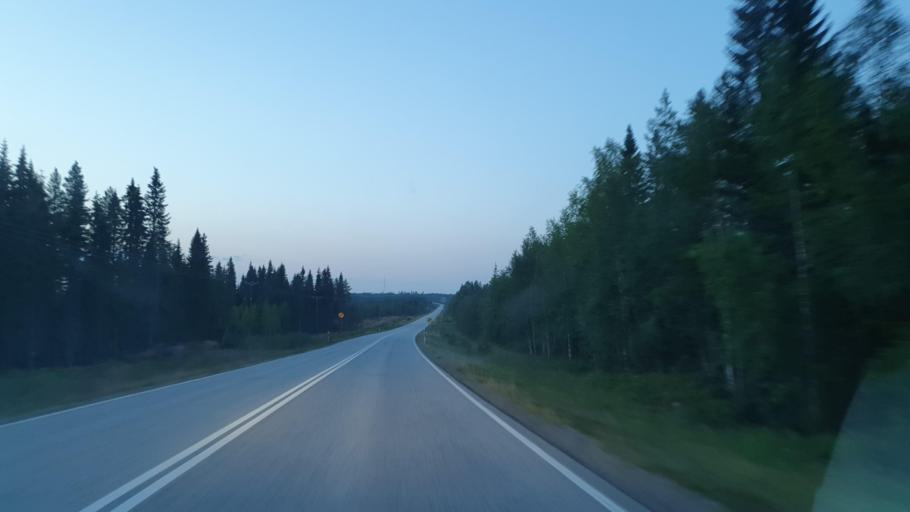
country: FI
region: Kainuu
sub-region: Kehys-Kainuu
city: Suomussalmi
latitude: 65.2675
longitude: 29.0240
